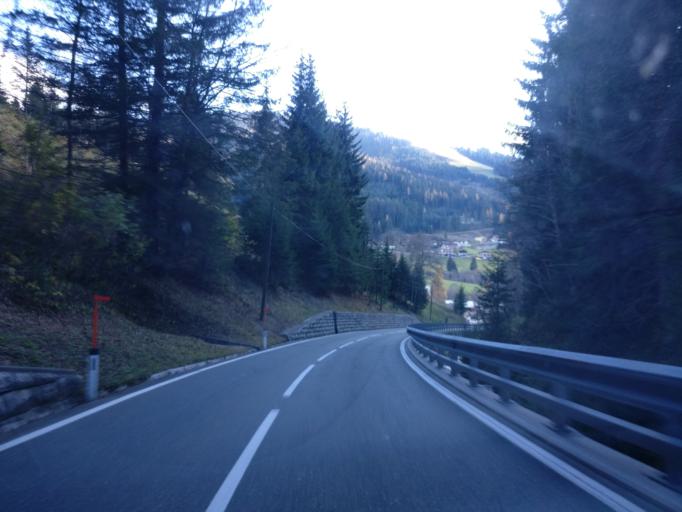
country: AT
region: Salzburg
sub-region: Politischer Bezirk Zell am See
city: Dienten am Hochkonig
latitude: 47.3922
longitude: 13.0155
